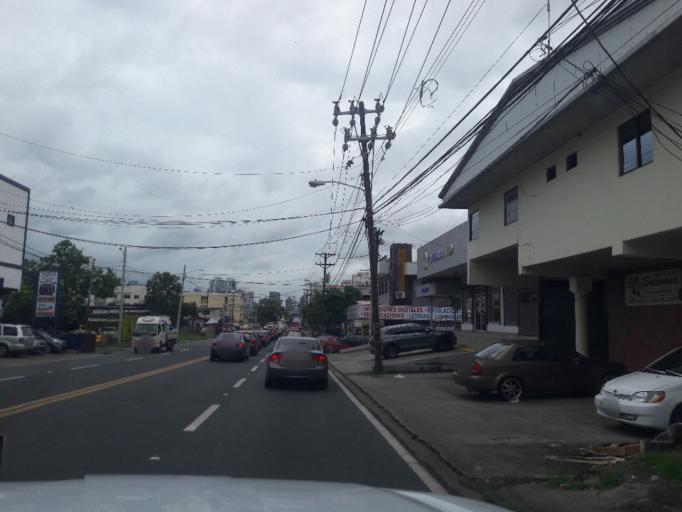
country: PA
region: Panama
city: Panama
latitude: 9.0097
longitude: -79.5212
